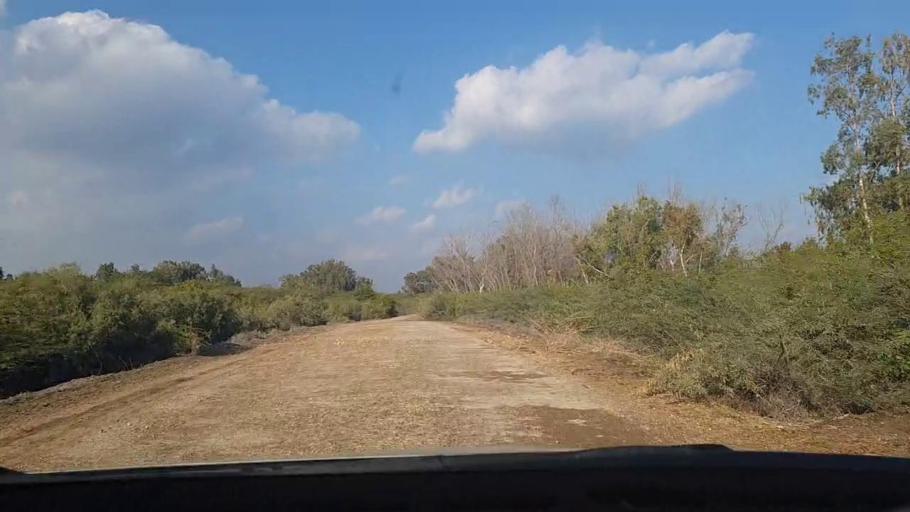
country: PK
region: Sindh
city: Tando Mittha Khan
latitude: 25.8989
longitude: 69.3023
